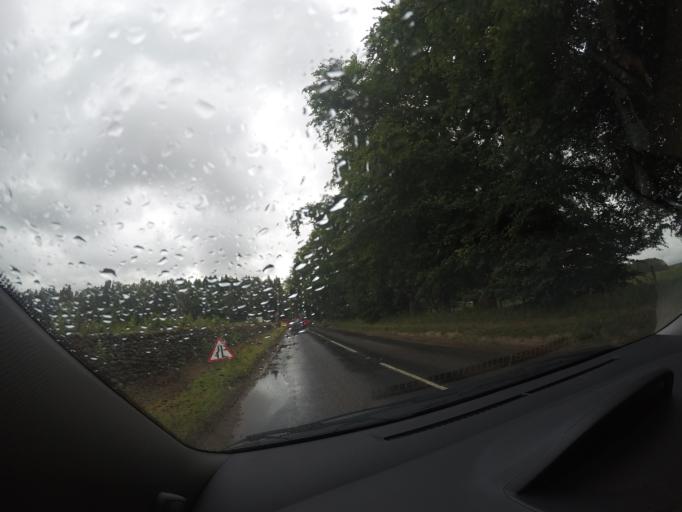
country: GB
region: Scotland
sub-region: Angus
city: Brechin
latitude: 56.7894
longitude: -2.6477
